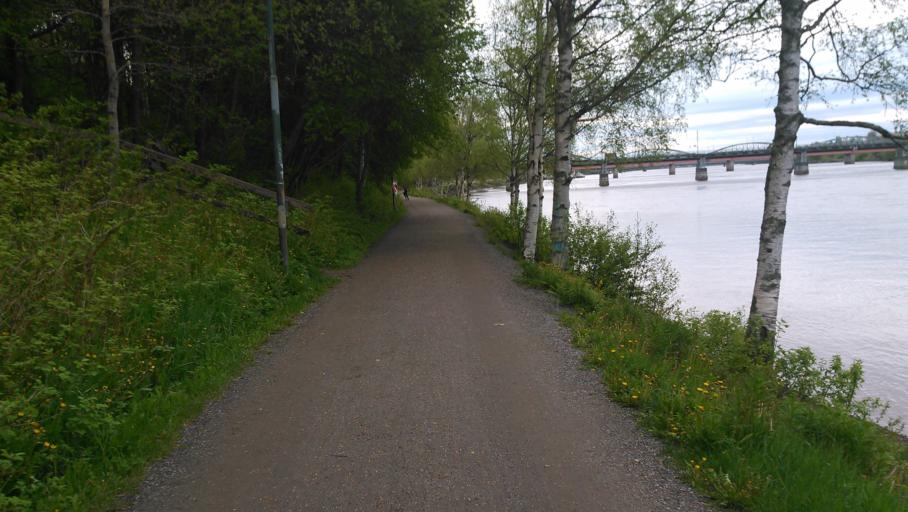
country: SE
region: Vaesterbotten
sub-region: Umea Kommun
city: Umea
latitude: 63.8267
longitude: 20.2445
